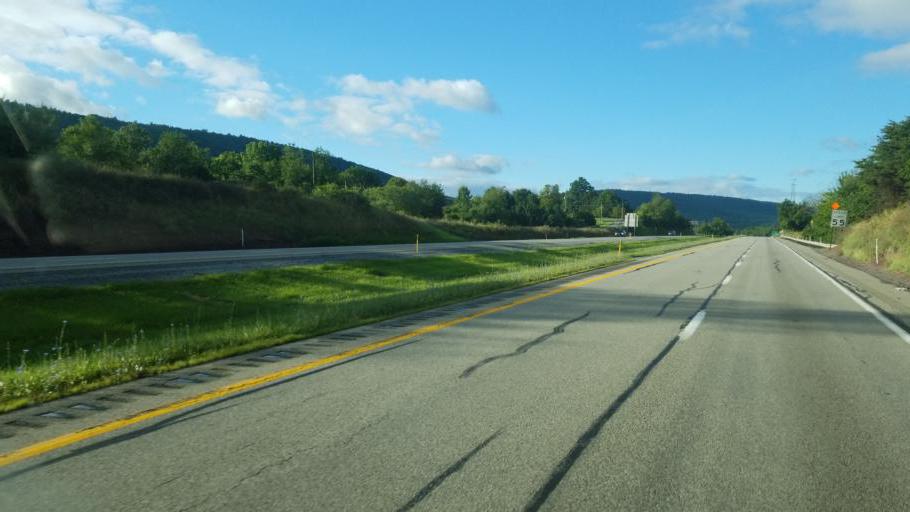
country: US
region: Pennsylvania
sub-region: Bedford County
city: Earlston
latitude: 39.9735
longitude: -78.2459
